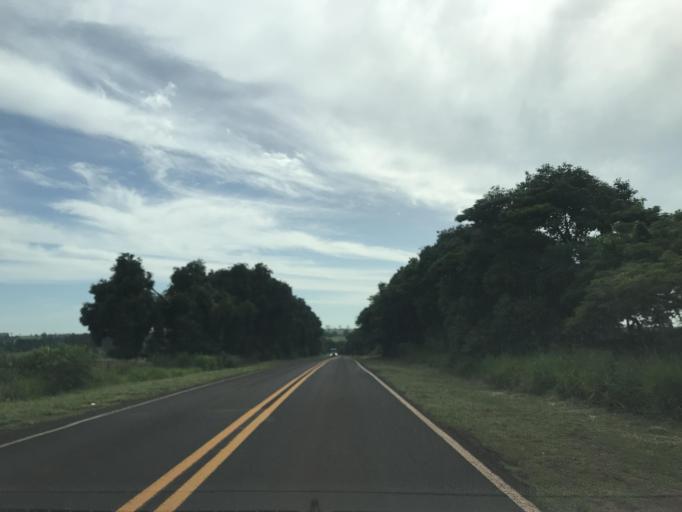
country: BR
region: Parana
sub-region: Terra Rica
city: Terra Rica
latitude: -22.7724
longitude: -52.6483
